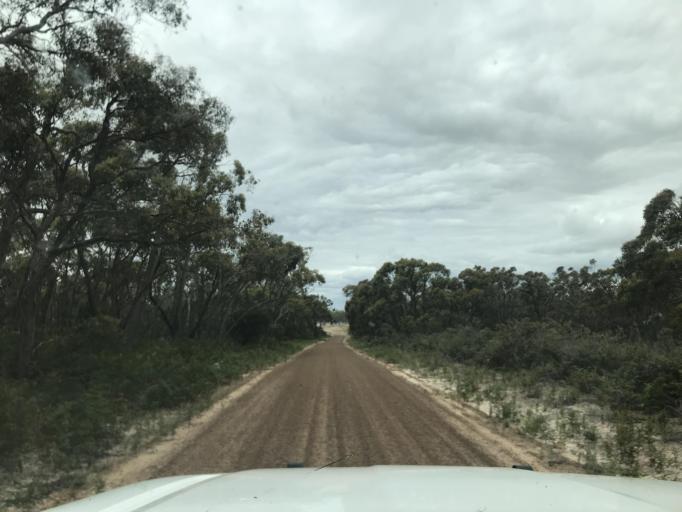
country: AU
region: South Australia
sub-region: Naracoorte and Lucindale
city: Naracoorte
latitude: -36.9225
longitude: 141.3294
